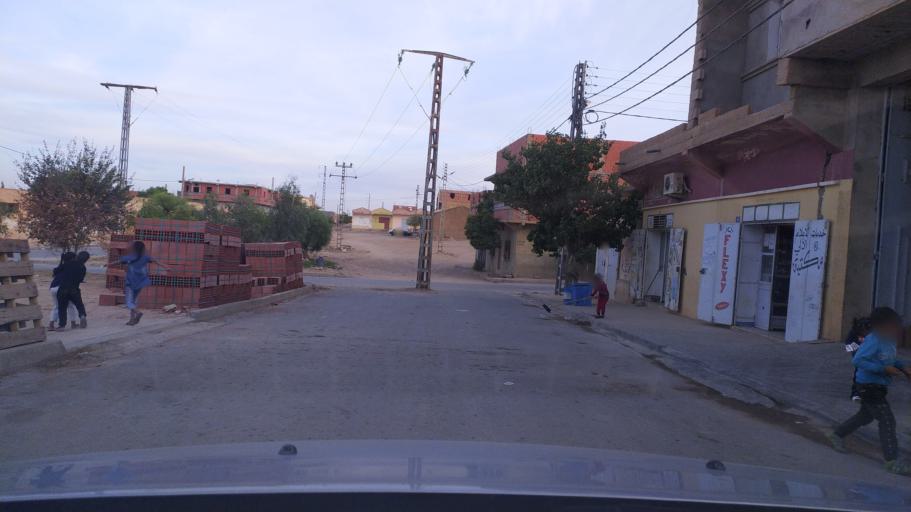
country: DZ
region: Tiaret
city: Frenda
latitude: 34.8931
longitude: 1.2411
